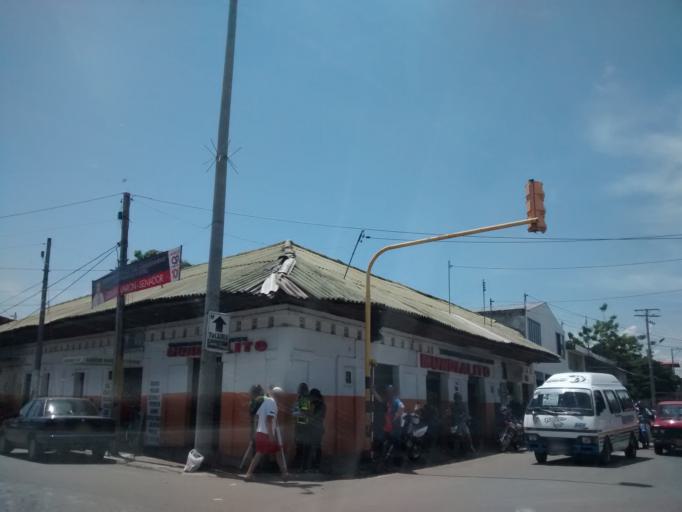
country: CO
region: Cundinamarca
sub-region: Girardot
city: Girardot City
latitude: 4.2993
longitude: -74.8007
